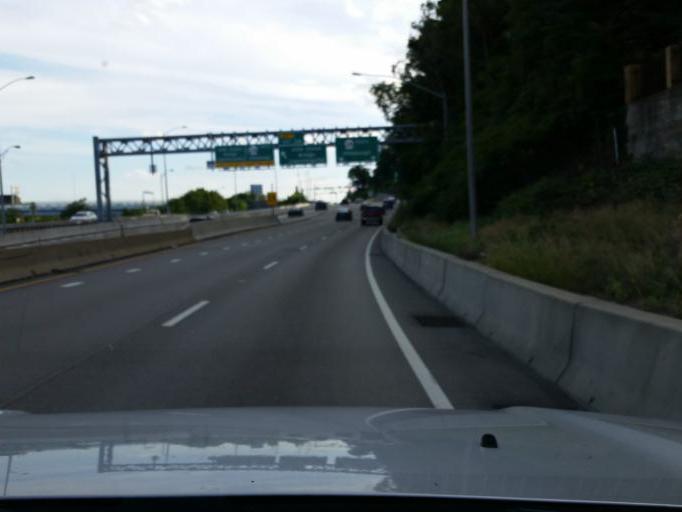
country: US
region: Pennsylvania
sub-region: Allegheny County
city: Millvale
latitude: 40.4766
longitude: -79.9695
